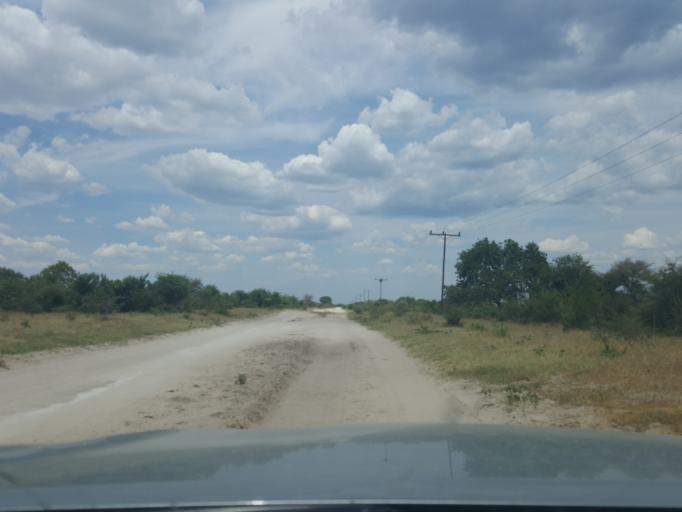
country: BW
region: North West
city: Shakawe
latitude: -18.5009
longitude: 22.1340
